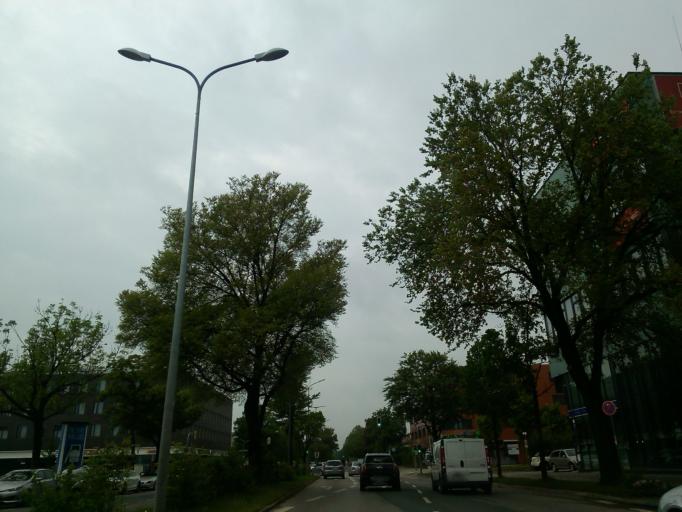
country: DE
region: Bavaria
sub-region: Upper Bavaria
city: Neubiberg
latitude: 48.1220
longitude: 11.6630
